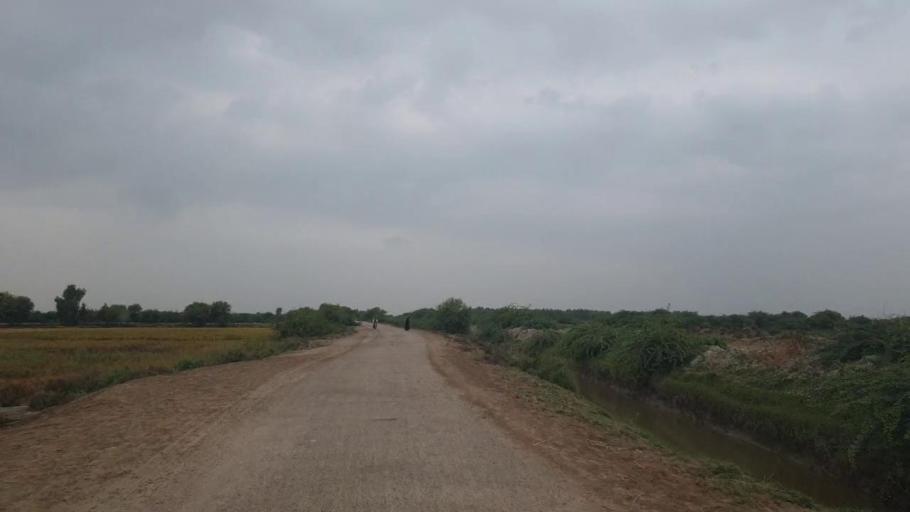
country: PK
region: Sindh
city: Badin
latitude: 24.6358
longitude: 68.6820
